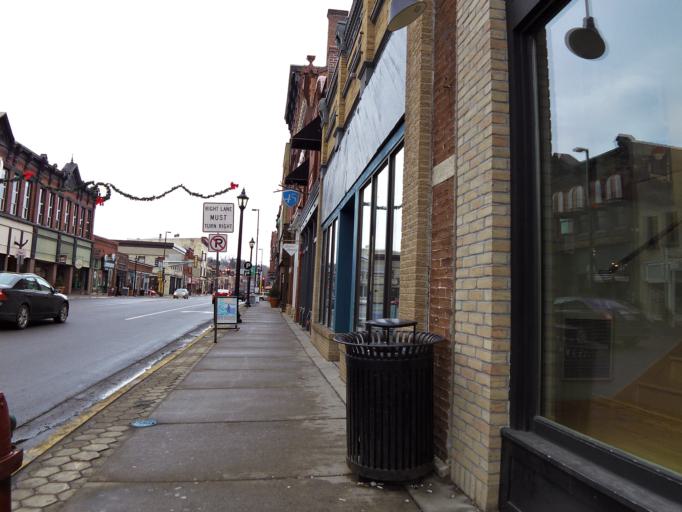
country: US
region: Minnesota
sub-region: Washington County
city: Stillwater
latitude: 45.0551
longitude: -92.8054
